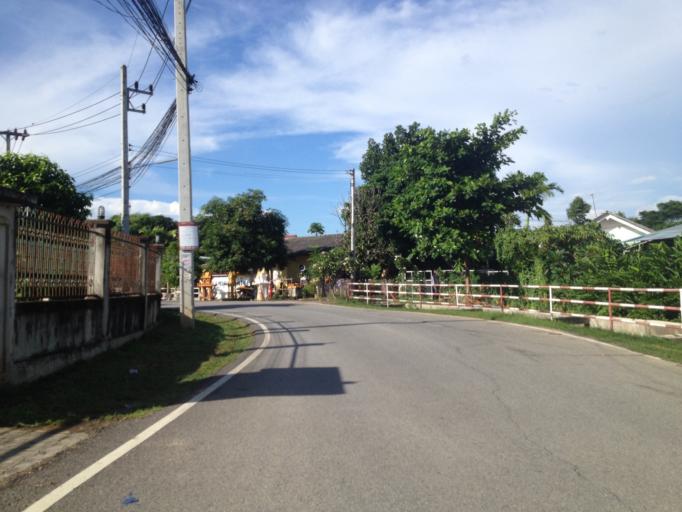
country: TH
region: Chiang Mai
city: Hang Dong
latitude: 18.7008
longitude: 98.9127
